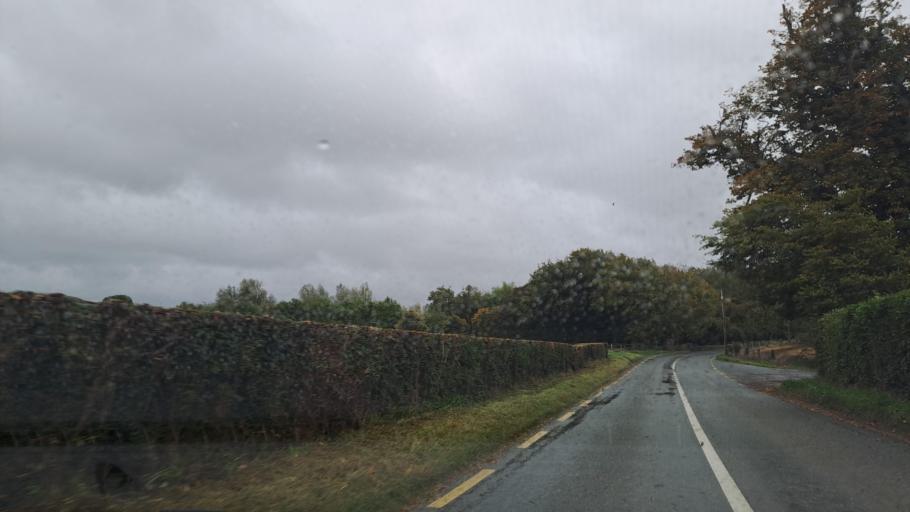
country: IE
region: Leinster
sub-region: Lu
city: Dundalk
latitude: 53.9631
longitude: -6.4617
